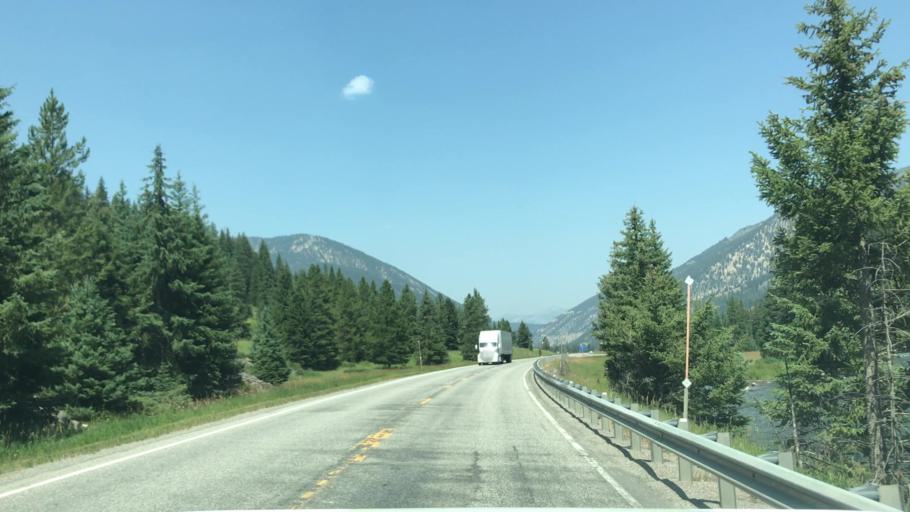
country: US
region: Montana
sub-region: Gallatin County
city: Big Sky
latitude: 45.0888
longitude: -111.2127
